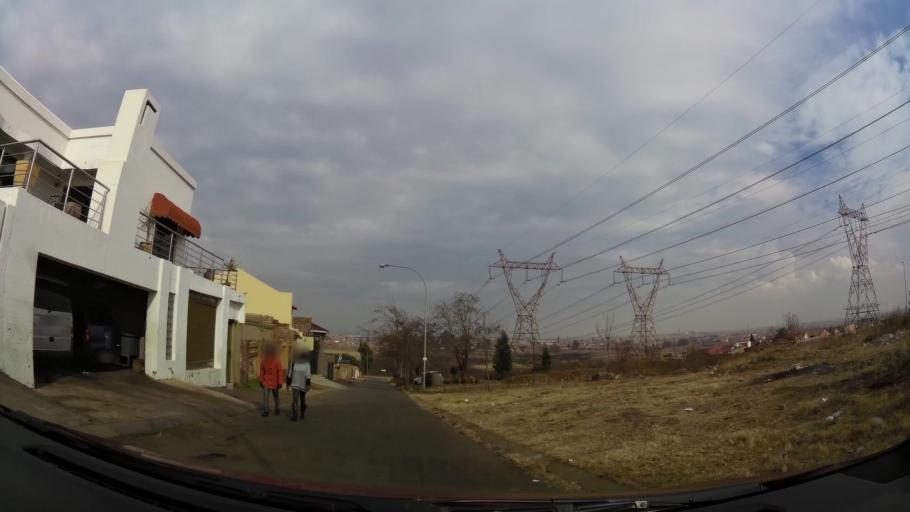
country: ZA
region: Gauteng
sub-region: City of Johannesburg Metropolitan Municipality
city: Soweto
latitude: -26.2665
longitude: 27.8259
